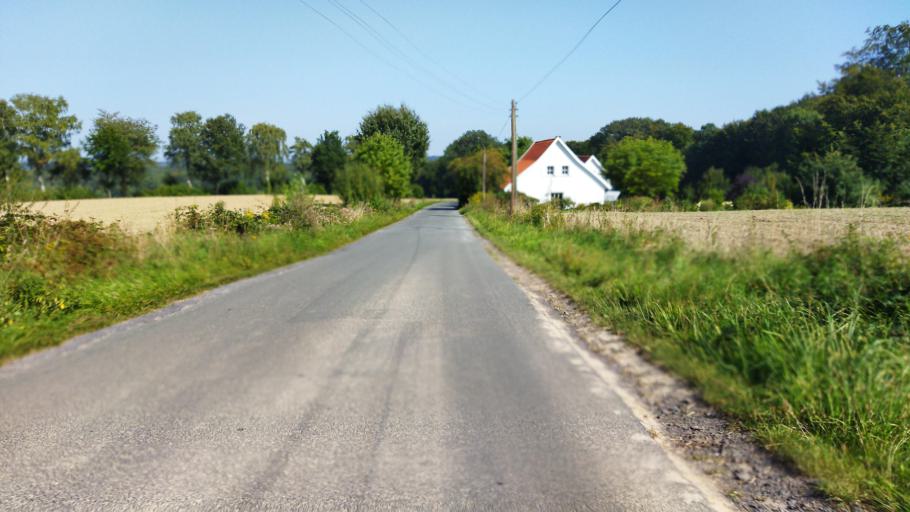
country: DE
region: North Rhine-Westphalia
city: Lengerich
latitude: 52.2236
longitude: 7.8579
